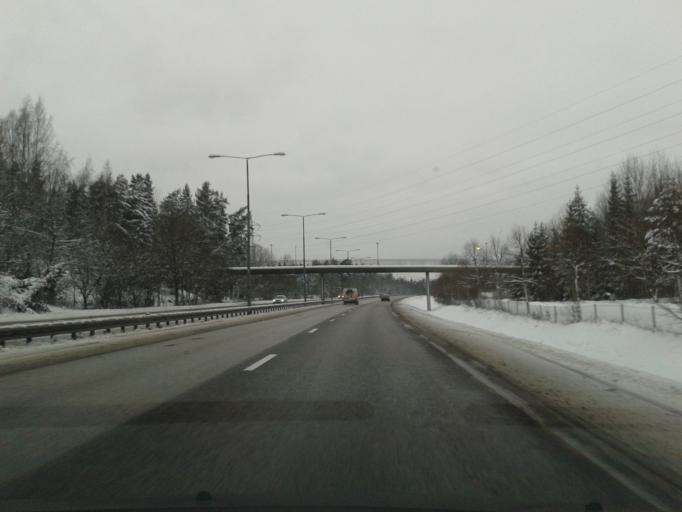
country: SE
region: Stockholm
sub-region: Stockholms Kommun
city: Arsta
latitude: 59.2593
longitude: 18.0744
